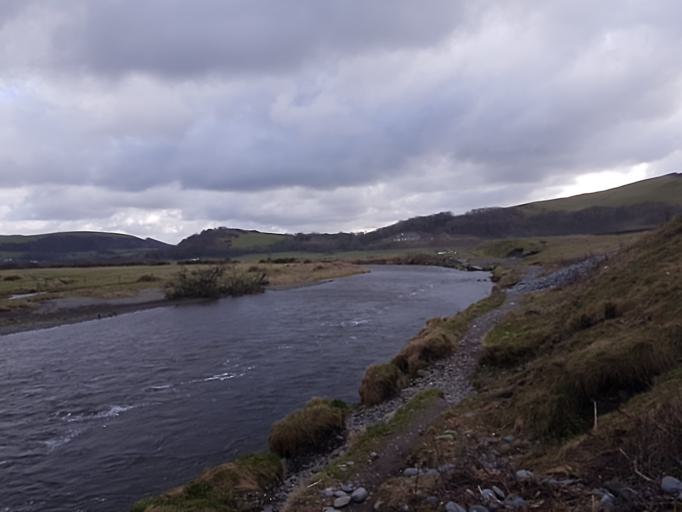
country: GB
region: Wales
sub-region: County of Ceredigion
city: Penparcau
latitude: 52.4011
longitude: -4.0880
